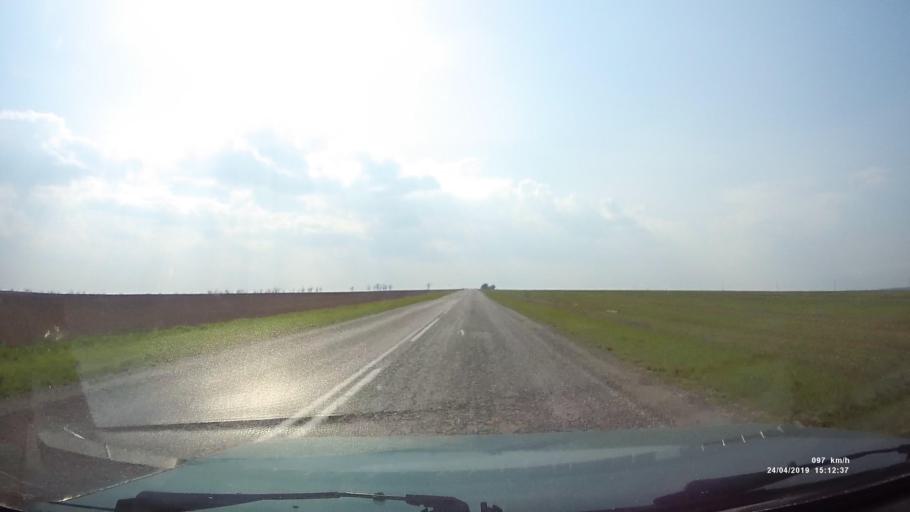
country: RU
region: Rostov
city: Remontnoye
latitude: 46.5464
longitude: 43.2967
